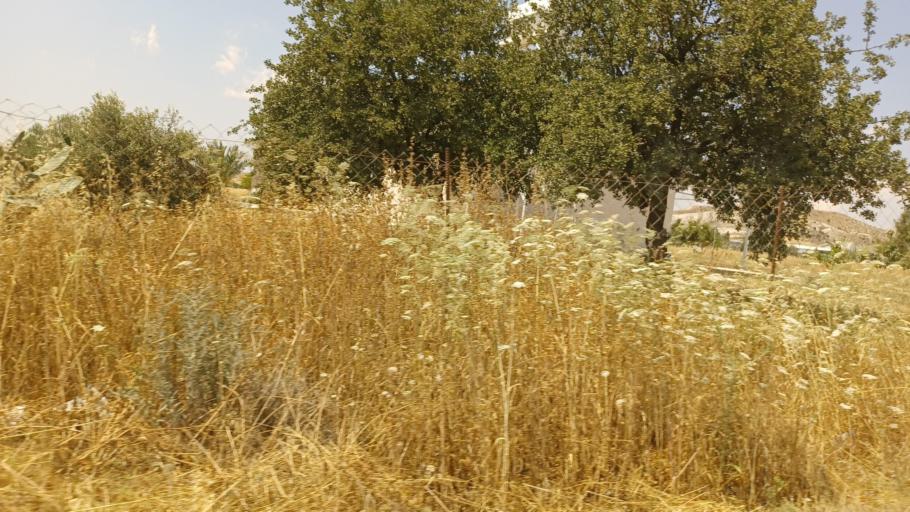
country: CY
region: Larnaka
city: Voroklini
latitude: 35.0061
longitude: 33.6512
